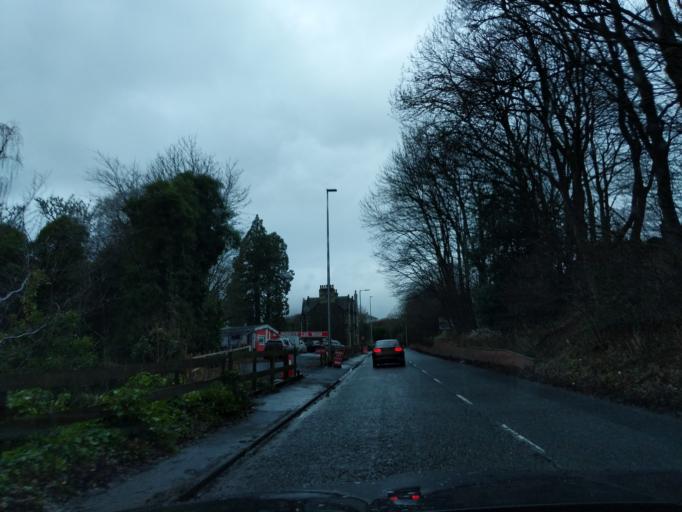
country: GB
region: Scotland
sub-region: The Scottish Borders
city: Galashiels
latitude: 55.6274
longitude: -2.8265
